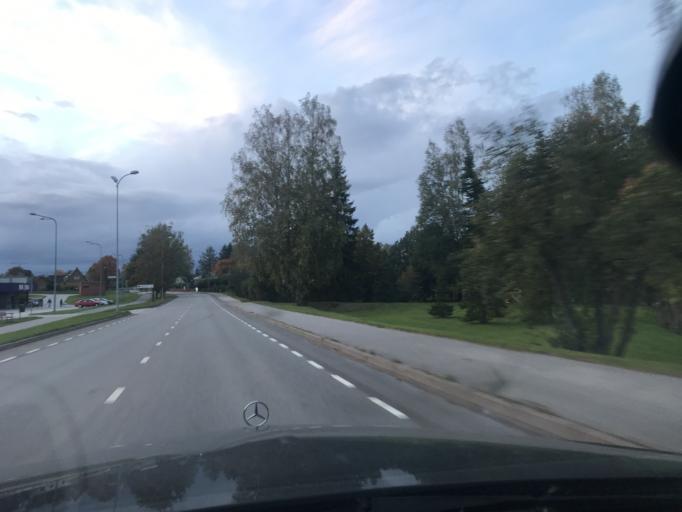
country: EE
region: Valgamaa
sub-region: Torva linn
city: Torva
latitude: 57.9972
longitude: 25.9344
